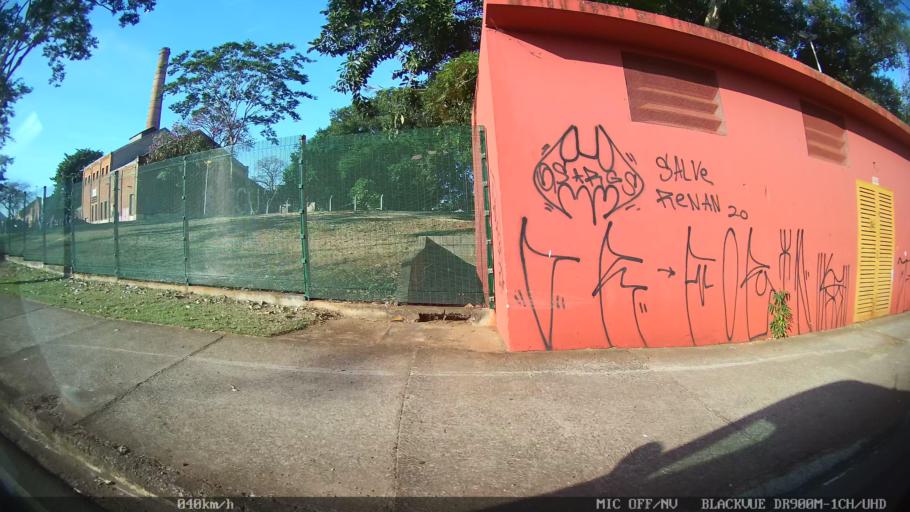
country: BR
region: Sao Paulo
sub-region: Sao Jose Do Rio Preto
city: Sao Jose do Rio Preto
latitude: -20.8101
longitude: -49.3702
